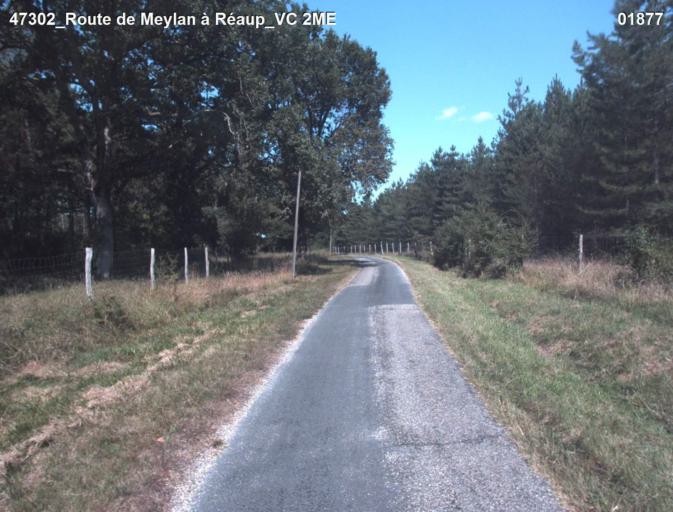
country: FR
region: Aquitaine
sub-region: Departement du Lot-et-Garonne
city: Mezin
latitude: 44.0929
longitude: 0.1298
